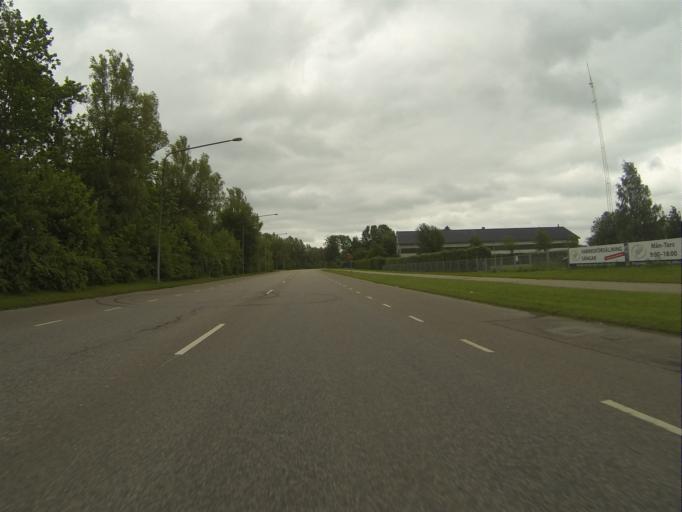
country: SE
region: Skane
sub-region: Staffanstorps Kommun
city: Staffanstorp
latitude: 55.6440
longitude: 13.1861
